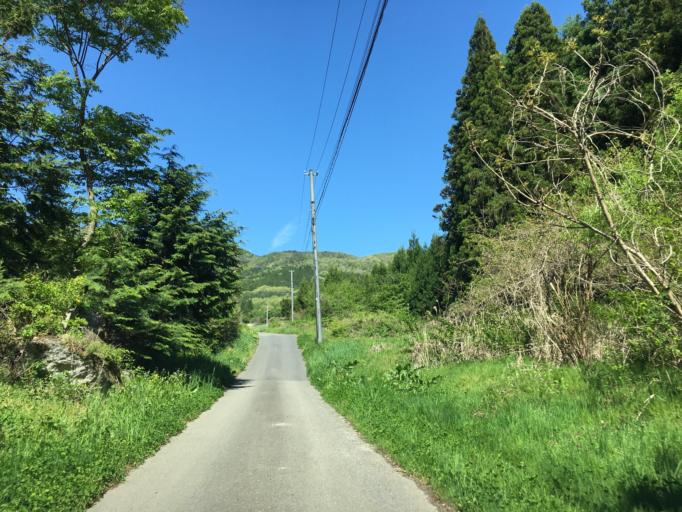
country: JP
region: Fukushima
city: Funehikimachi-funehiki
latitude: 37.3030
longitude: 140.6739
